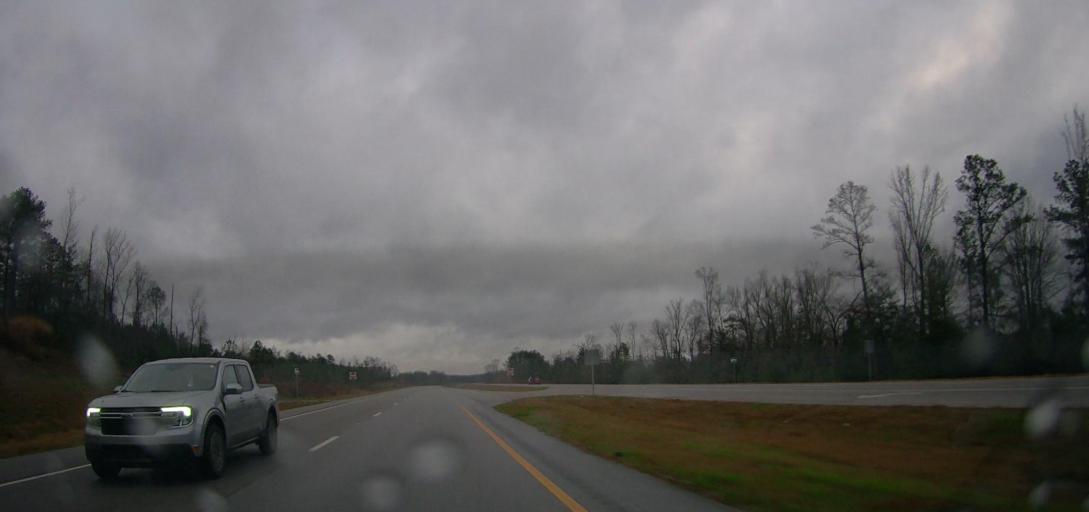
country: US
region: Alabama
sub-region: Bibb County
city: Centreville
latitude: 32.9437
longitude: -87.0833
